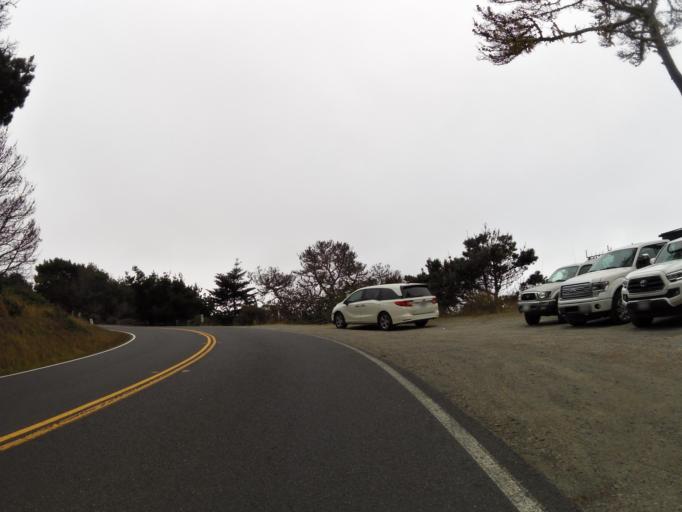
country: US
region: California
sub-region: Sonoma County
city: Sea Ranch
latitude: 38.5470
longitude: -123.2969
